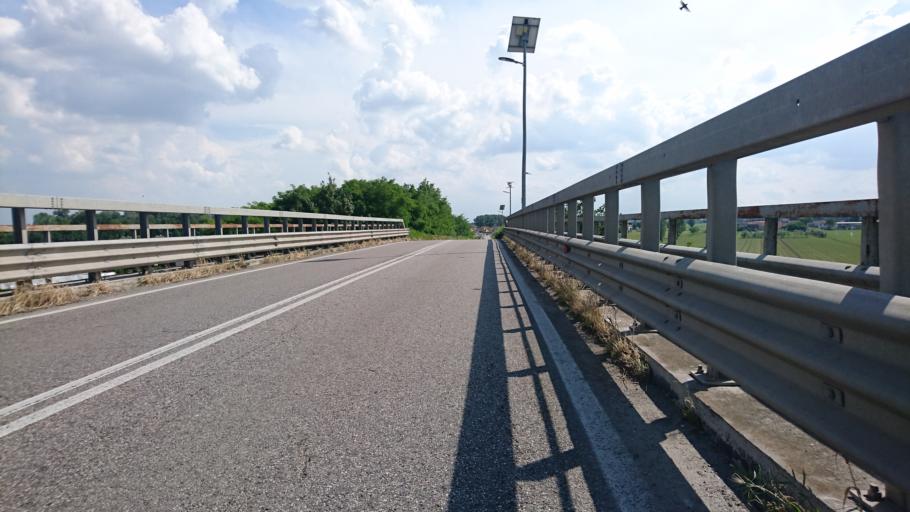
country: IT
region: Lombardy
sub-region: Provincia di Mantova
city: Sermide
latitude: 45.0134
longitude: 11.2891
